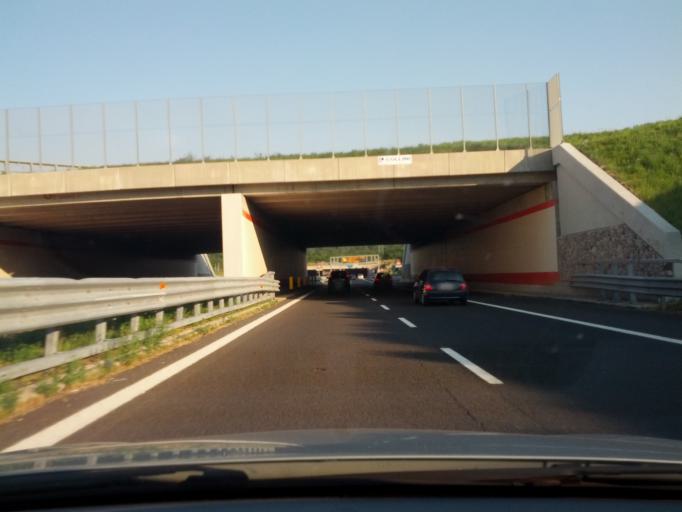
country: IT
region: Friuli Venezia Giulia
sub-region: Provincia di Trieste
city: Trieste
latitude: 45.6592
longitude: 13.8316
